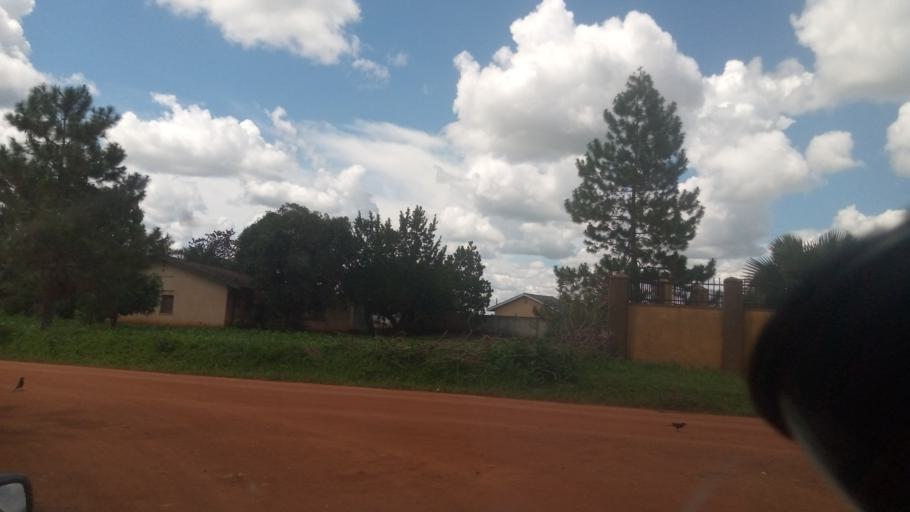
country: UG
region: Northern Region
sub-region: Lira District
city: Lira
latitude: 2.2397
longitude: 32.9040
